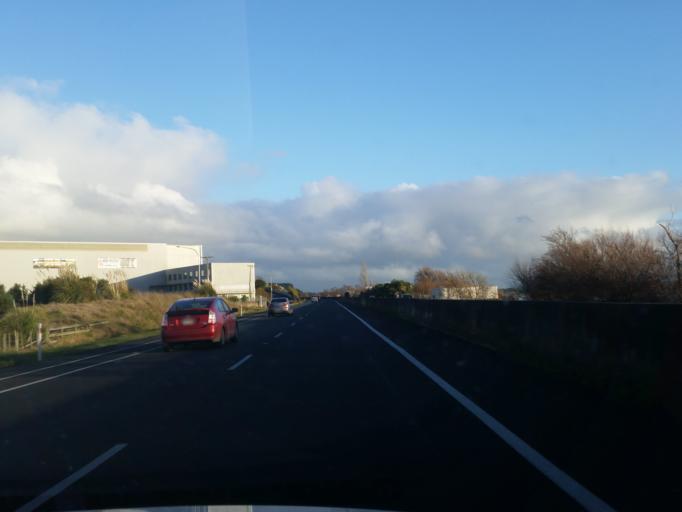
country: NZ
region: Waikato
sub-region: Waikato District
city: Te Kauwhata
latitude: -37.3115
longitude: 175.0672
